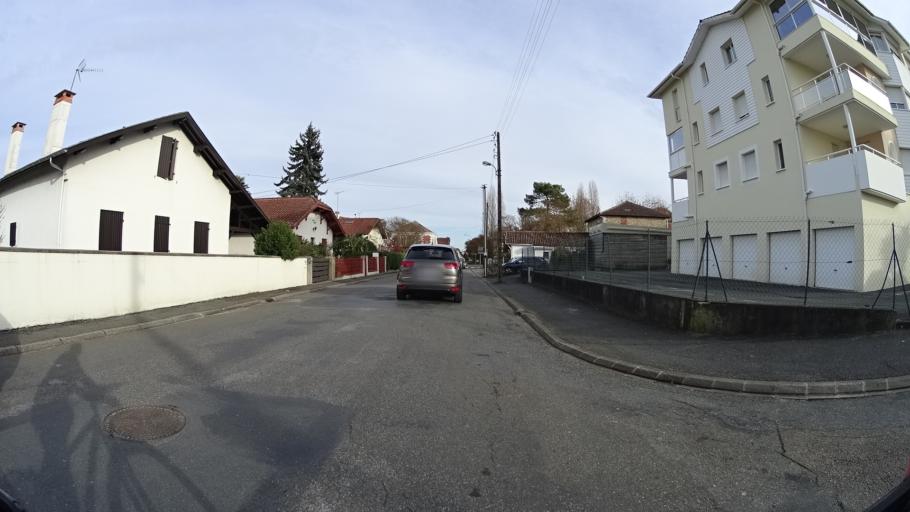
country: FR
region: Aquitaine
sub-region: Departement des Landes
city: Saint-Paul-les-Dax
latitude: 43.7309
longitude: -1.0497
